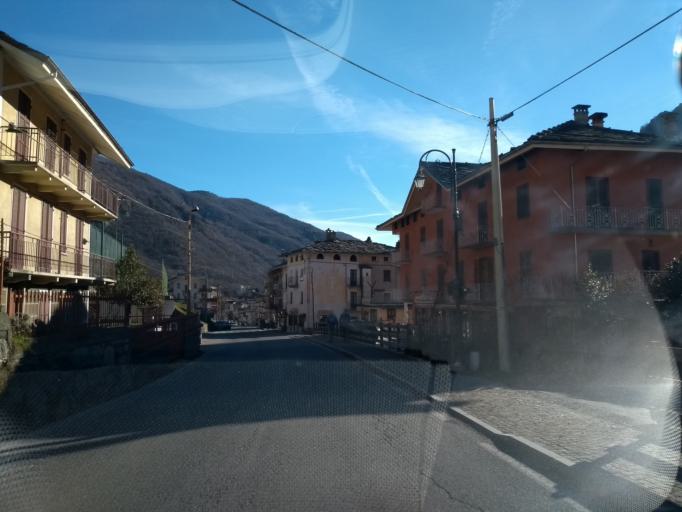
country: IT
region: Piedmont
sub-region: Provincia di Torino
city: Cantoira
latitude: 45.3439
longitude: 7.3787
